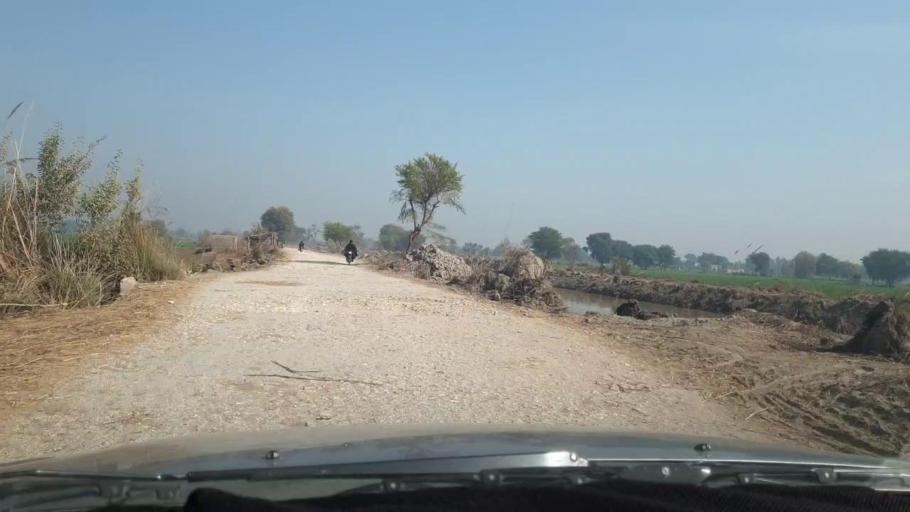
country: PK
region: Sindh
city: Khanpur
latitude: 27.7911
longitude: 69.5596
